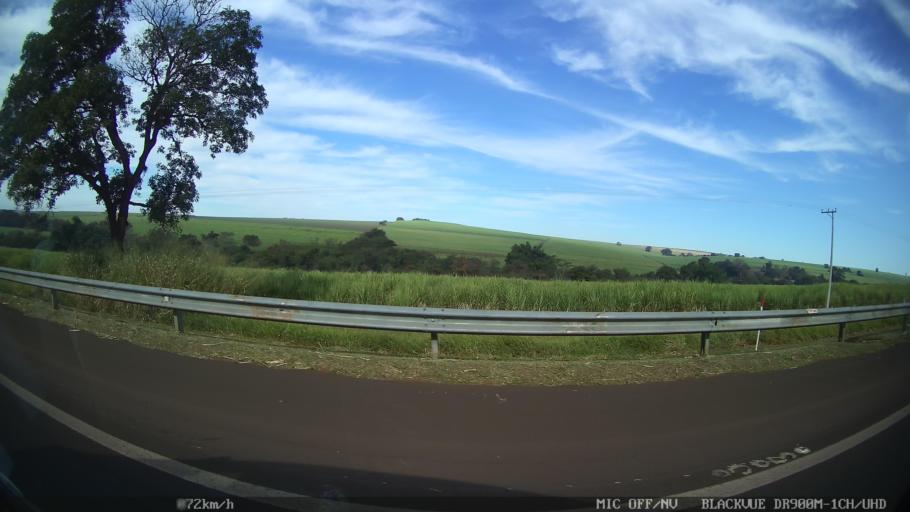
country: BR
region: Sao Paulo
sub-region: Americo Brasiliense
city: Americo Brasiliense
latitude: -21.7603
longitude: -48.0761
